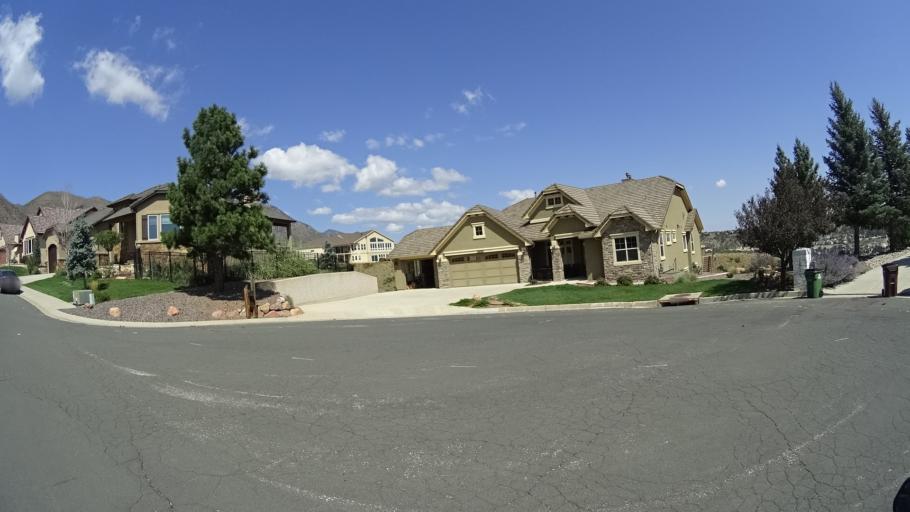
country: US
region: Colorado
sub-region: El Paso County
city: Air Force Academy
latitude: 38.9240
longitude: -104.8754
